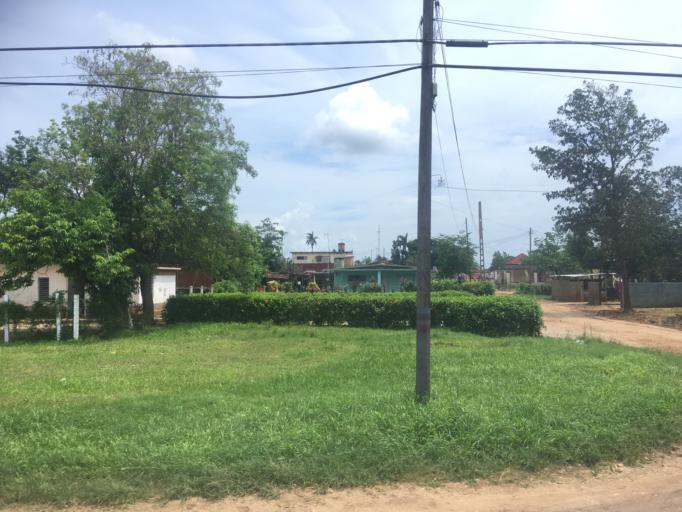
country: CU
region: Matanzas
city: Perico
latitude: 22.7741
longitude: -81.0280
